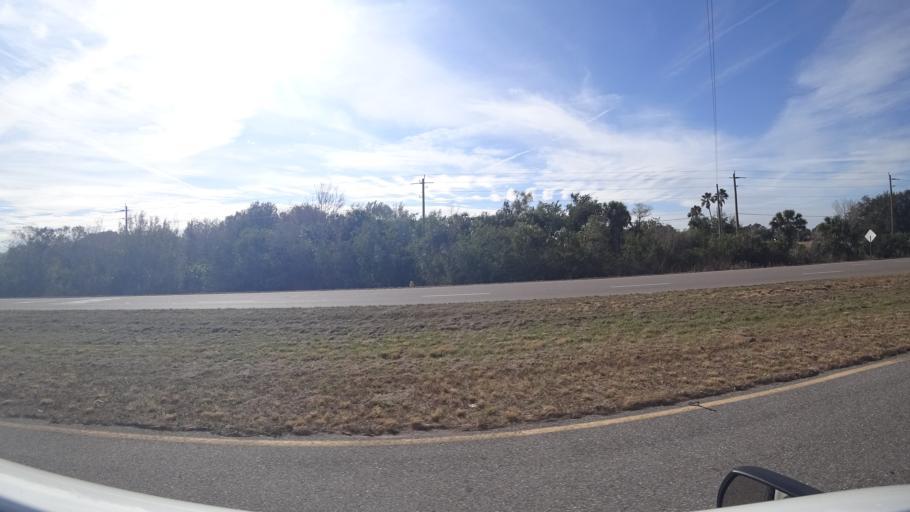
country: US
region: Florida
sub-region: Manatee County
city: Ellenton
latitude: 27.6012
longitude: -82.4953
